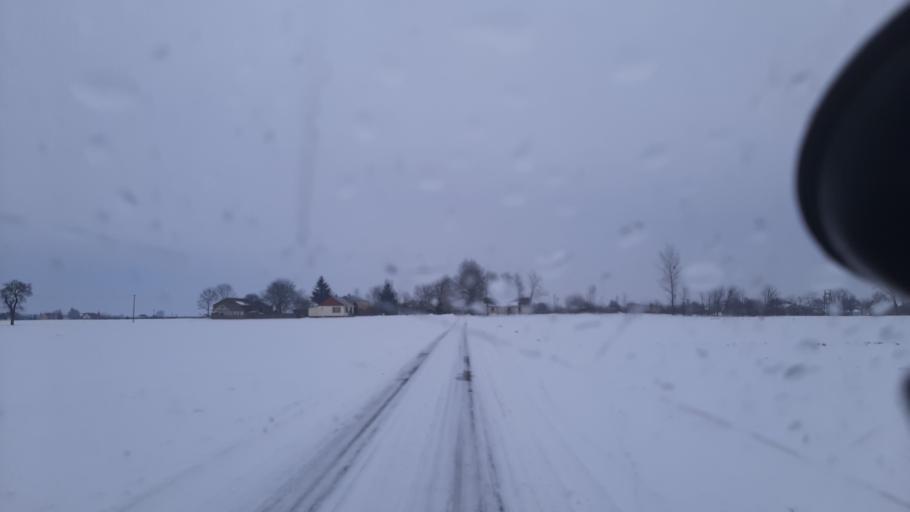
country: PL
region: Lublin Voivodeship
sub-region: Powiat lubelski
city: Garbow
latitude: 51.3554
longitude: 22.3912
